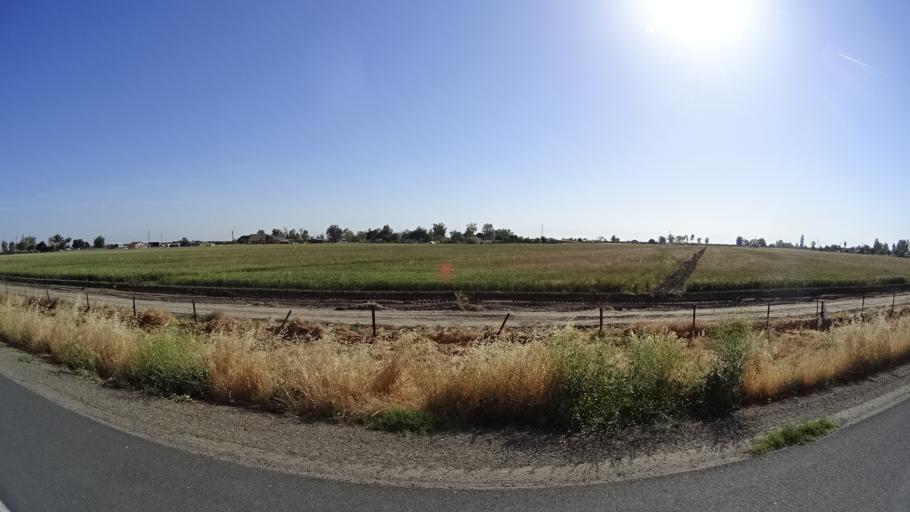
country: US
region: California
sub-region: Kings County
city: Corcoran
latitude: 36.1176
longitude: -119.5704
